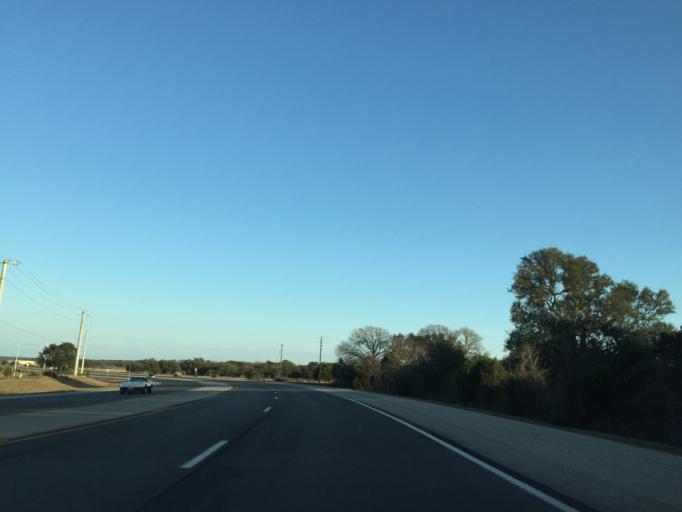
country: US
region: Texas
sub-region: Williamson County
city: Florence
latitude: 30.7354
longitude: -97.7966
